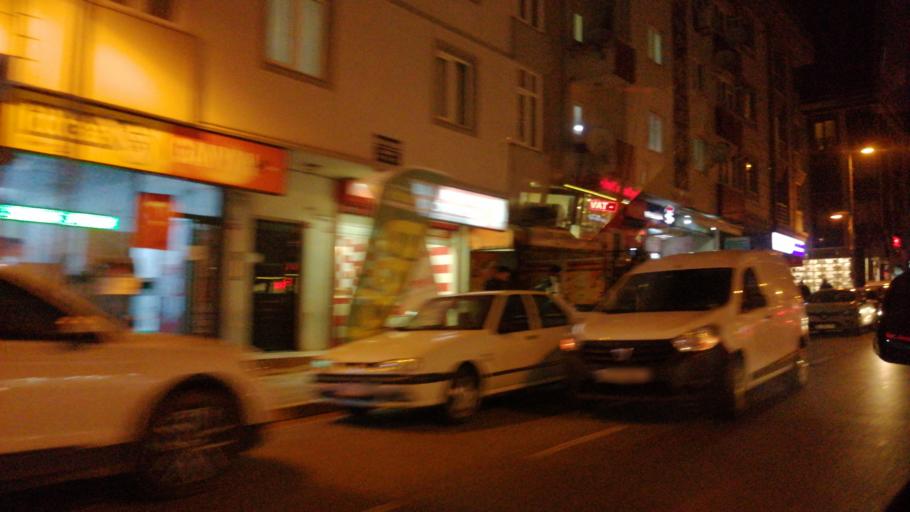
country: TR
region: Istanbul
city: Umraniye
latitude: 41.0120
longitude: 29.1280
